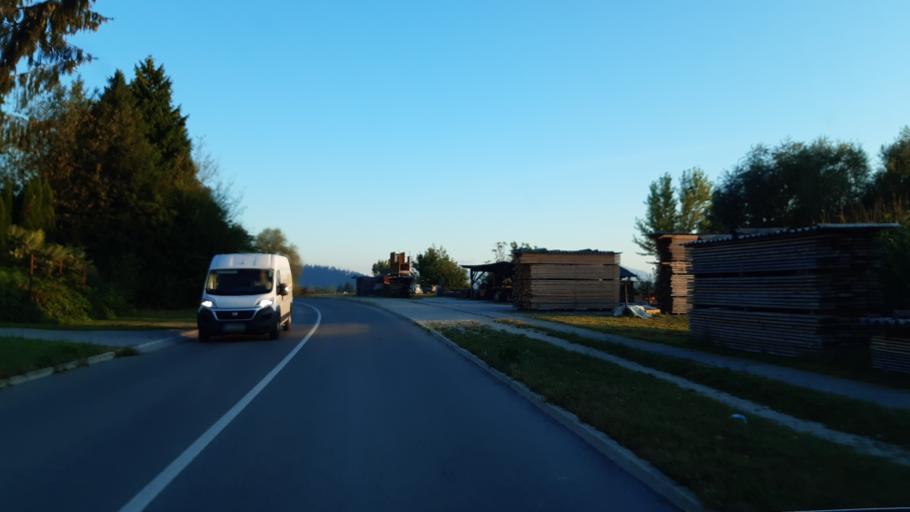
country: SI
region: Medvode
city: Zgornje Pirnice
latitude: 46.1047
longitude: 14.4440
